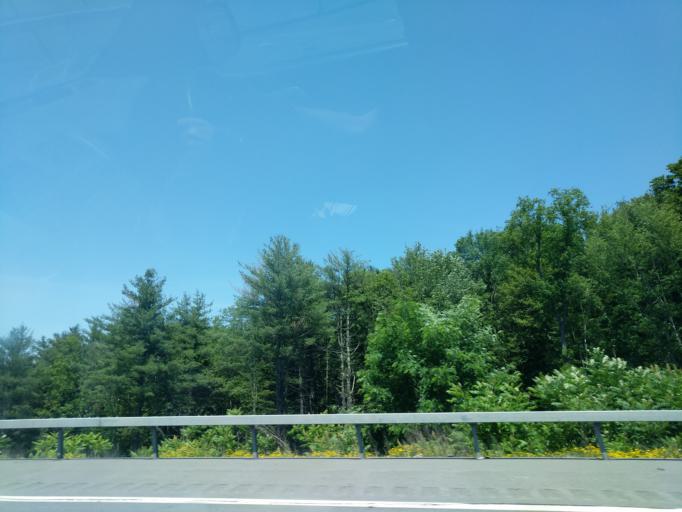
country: US
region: New York
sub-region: Sullivan County
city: Rock Hill
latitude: 41.6360
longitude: -74.6167
